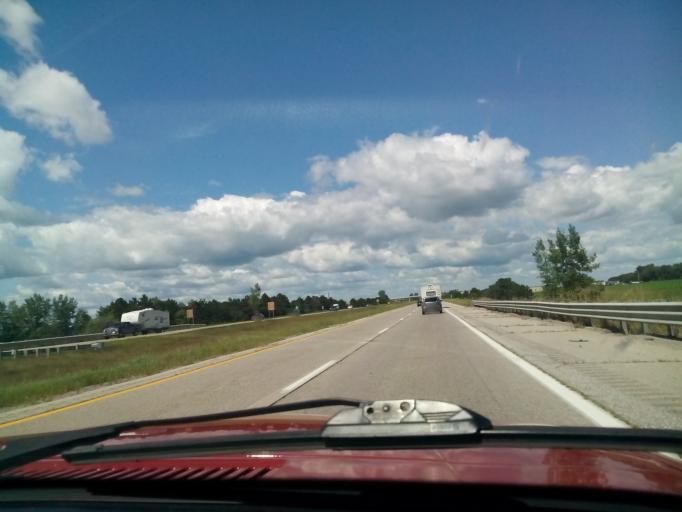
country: US
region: Michigan
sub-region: Bay County
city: Bay City
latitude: 43.6406
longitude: -83.9751
